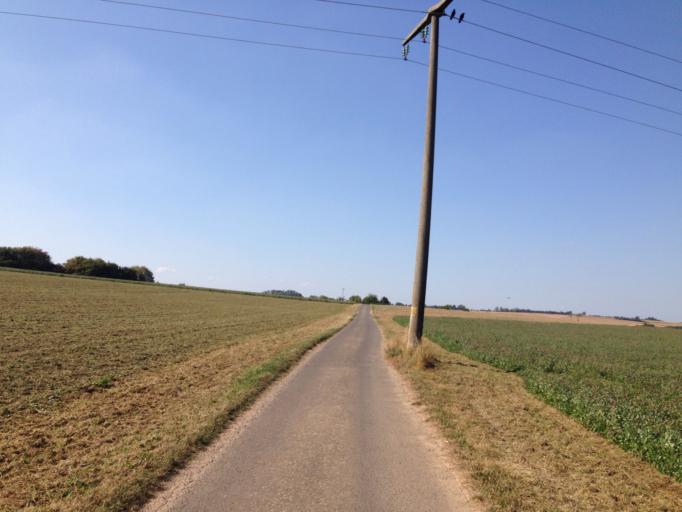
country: DE
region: Hesse
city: Staufenberg
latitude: 50.6536
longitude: 8.7527
